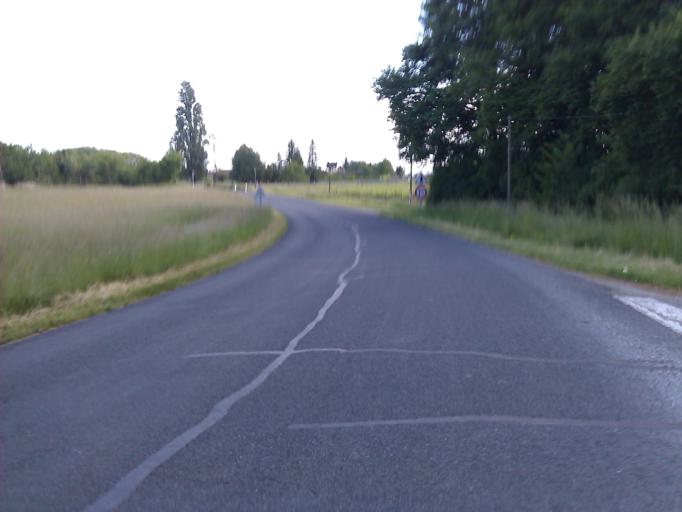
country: FR
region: Aquitaine
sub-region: Departement de la Gironde
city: Peujard
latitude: 45.0336
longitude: -0.4436
